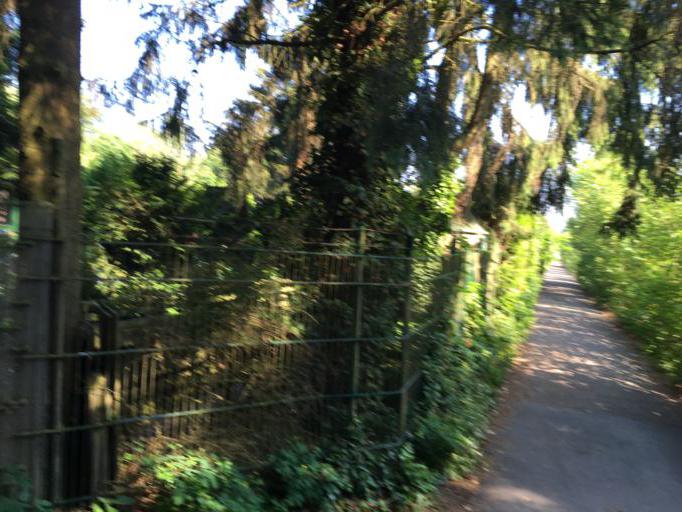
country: DE
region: Hesse
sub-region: Regierungsbezirk Darmstadt
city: Frankfurt am Main
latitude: 50.0898
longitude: 8.7197
